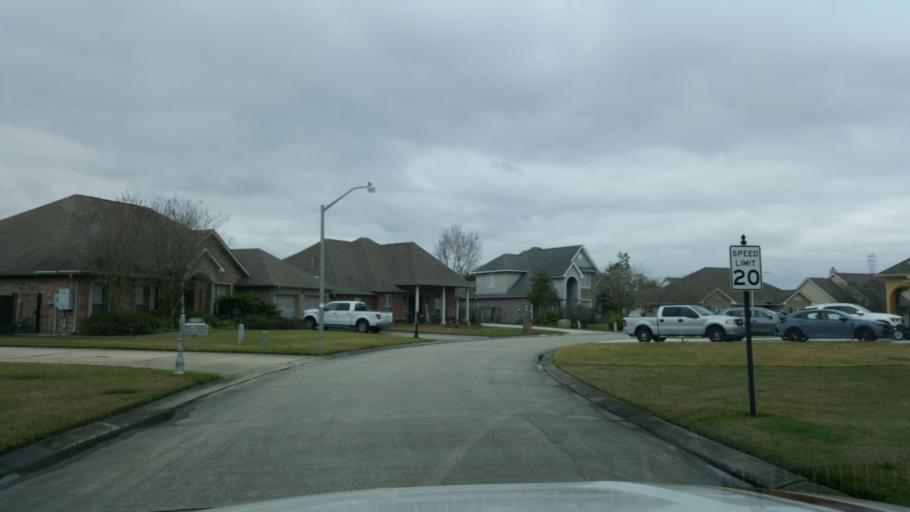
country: US
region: Louisiana
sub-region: Jefferson Parish
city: Woodmere
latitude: 29.8759
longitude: -90.0803
